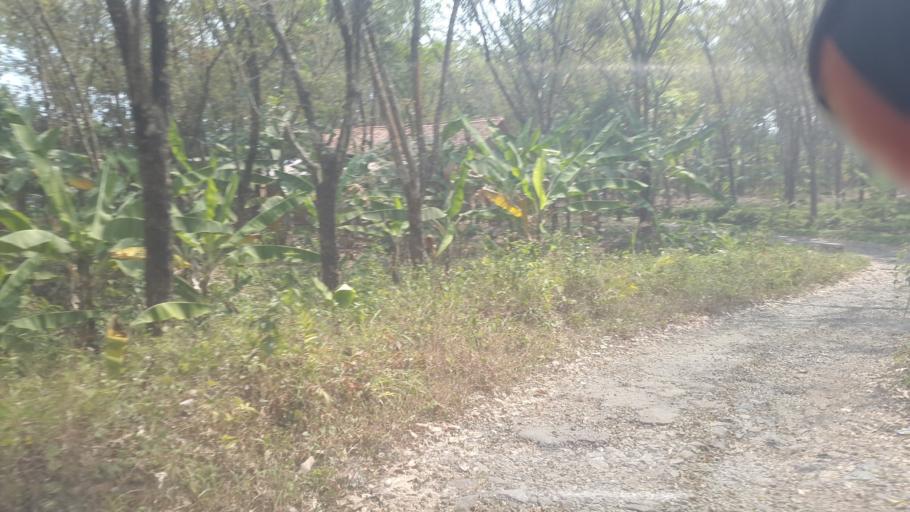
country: ID
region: West Java
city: Cimaja
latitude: -6.9348
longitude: 106.4985
